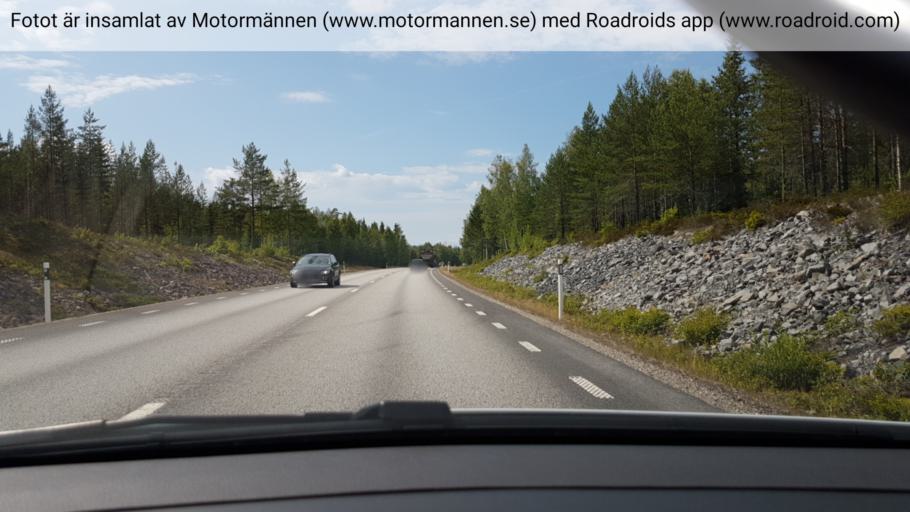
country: SE
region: Dalarna
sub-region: Faluns Kommun
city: Bjursas
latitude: 60.7851
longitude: 15.2970
